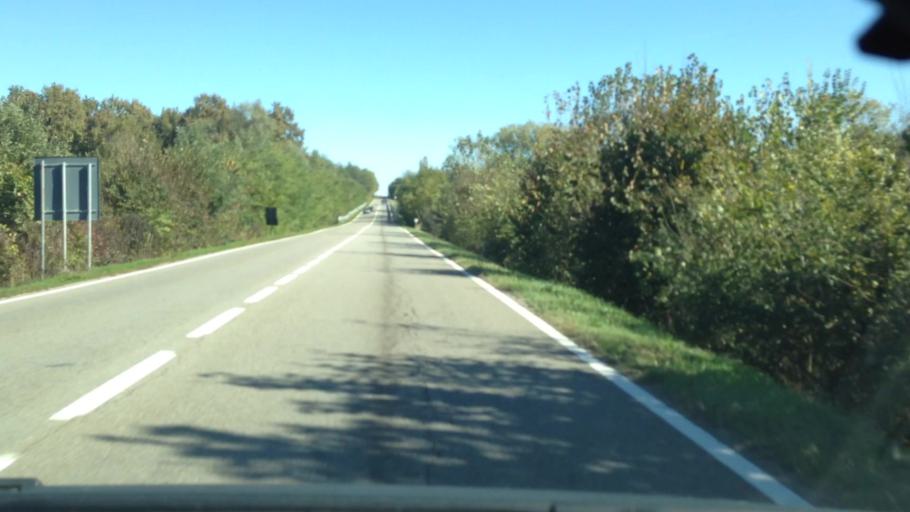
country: IT
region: Piedmont
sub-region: Provincia di Asti
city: Cerro Tanaro
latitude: 44.8810
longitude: 8.3422
